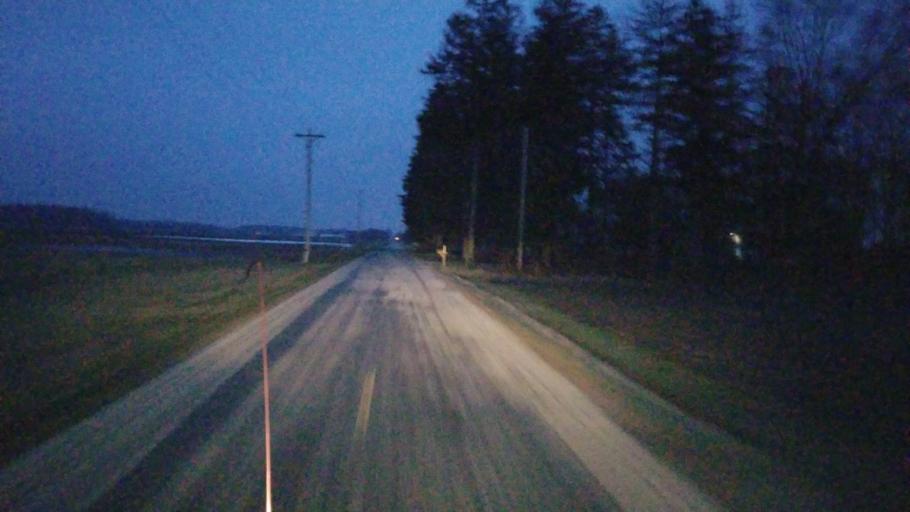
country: US
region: Ohio
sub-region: Delaware County
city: Ashley
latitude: 40.4990
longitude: -82.9917
